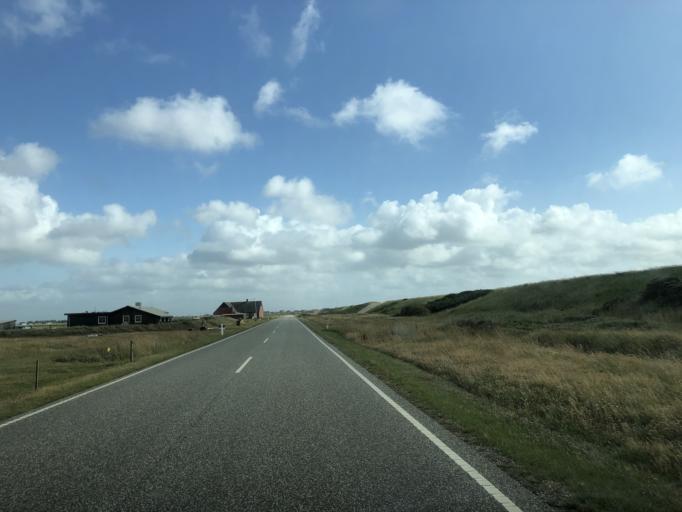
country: DK
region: Central Jutland
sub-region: Holstebro Kommune
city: Ulfborg
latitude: 56.3861
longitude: 8.1218
